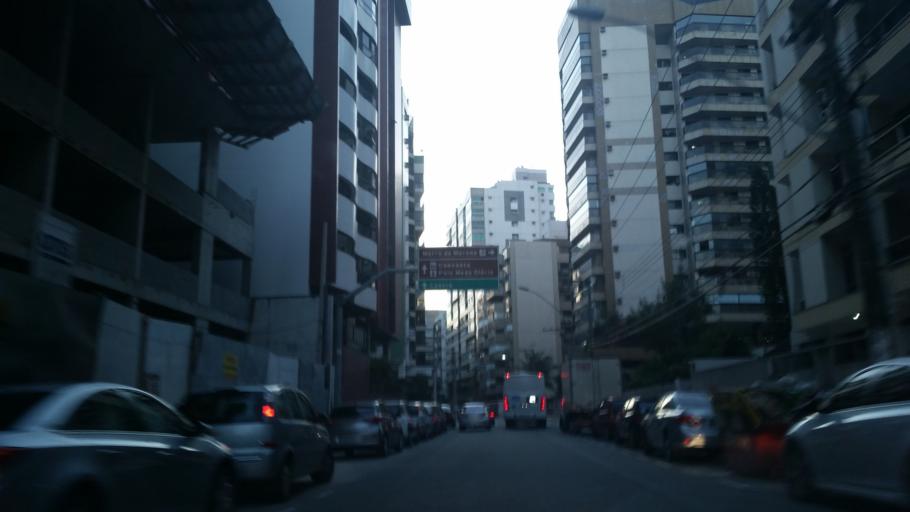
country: BR
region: Espirito Santo
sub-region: Vila Velha
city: Vila Velha
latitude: -20.3310
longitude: -40.2761
